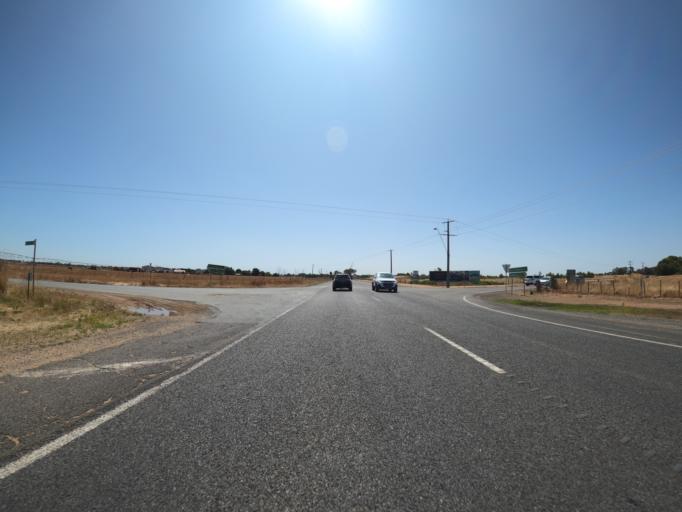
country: AU
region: Victoria
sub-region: Moira
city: Yarrawonga
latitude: -36.0177
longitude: 146.0494
